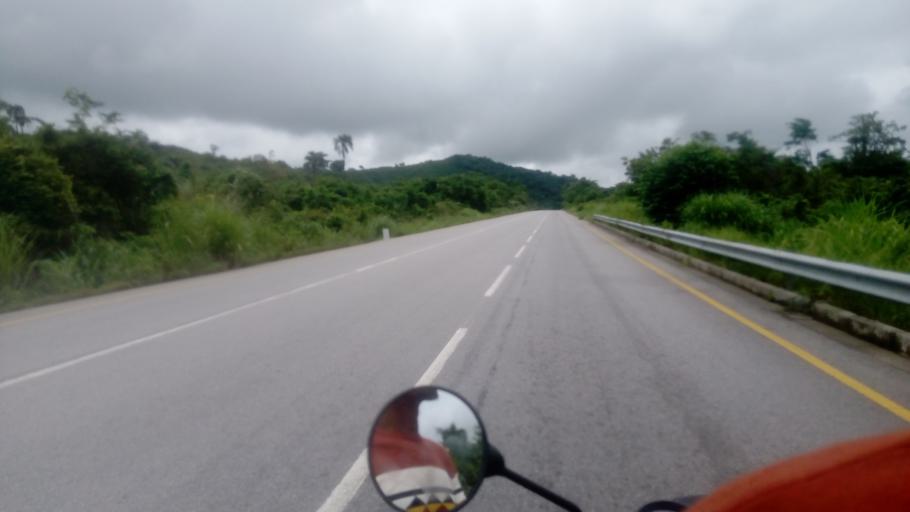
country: SL
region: Northern Province
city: Masaka
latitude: 8.6612
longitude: -11.7890
